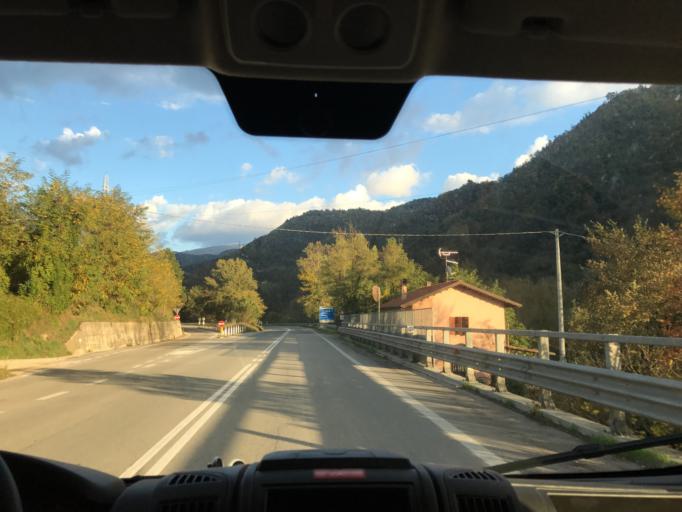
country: IT
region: The Marches
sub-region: Provincia di Ascoli Piceno
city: Marsia
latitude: 42.8023
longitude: 13.4694
